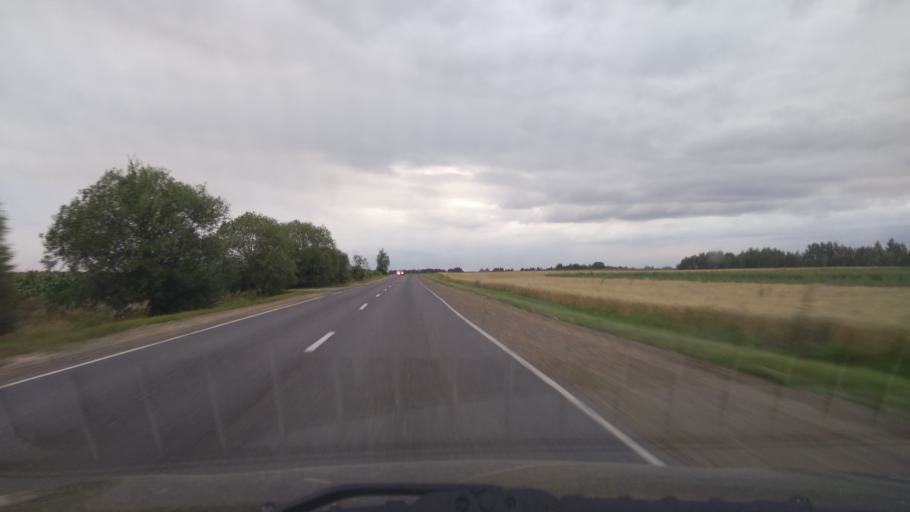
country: BY
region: Brest
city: Byaroza
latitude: 52.4279
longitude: 24.9807
